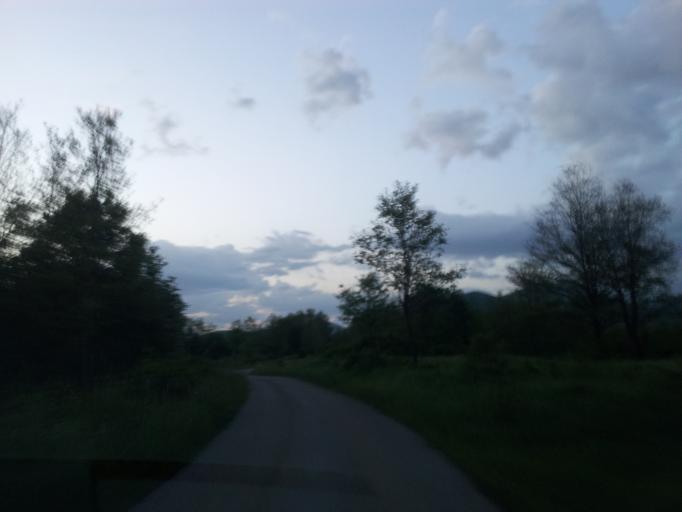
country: HR
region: Zadarska
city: Gracac
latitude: 44.3969
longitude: 15.6883
